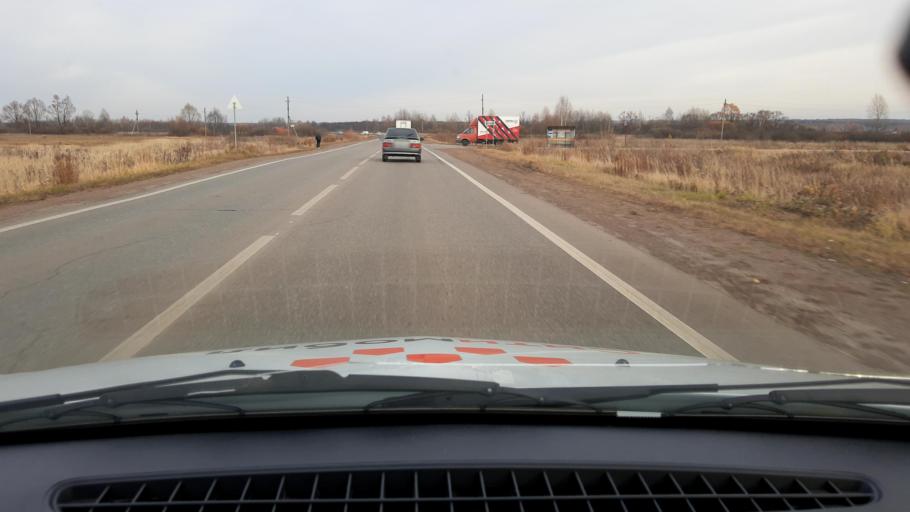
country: RU
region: Bashkortostan
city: Kabakovo
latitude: 54.7336
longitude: 56.1988
